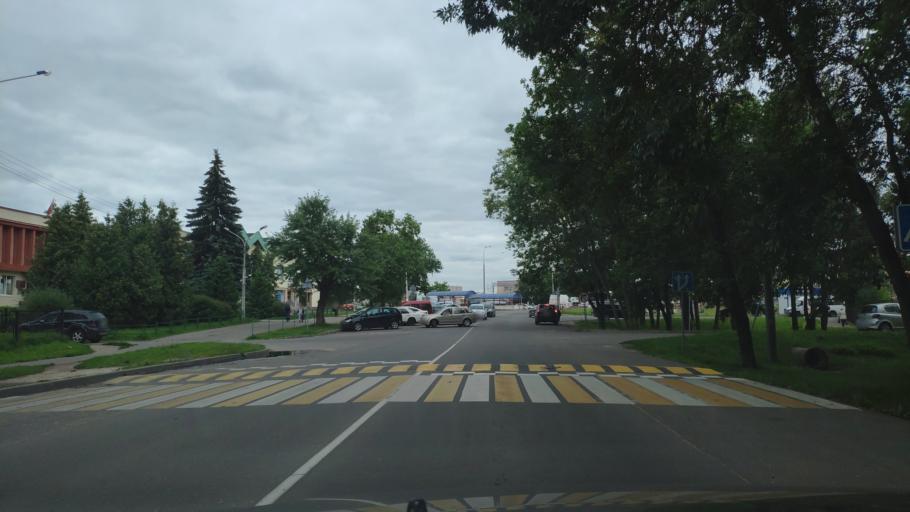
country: BY
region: Minsk
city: Zhdanovichy
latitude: 53.9488
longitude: 27.4285
